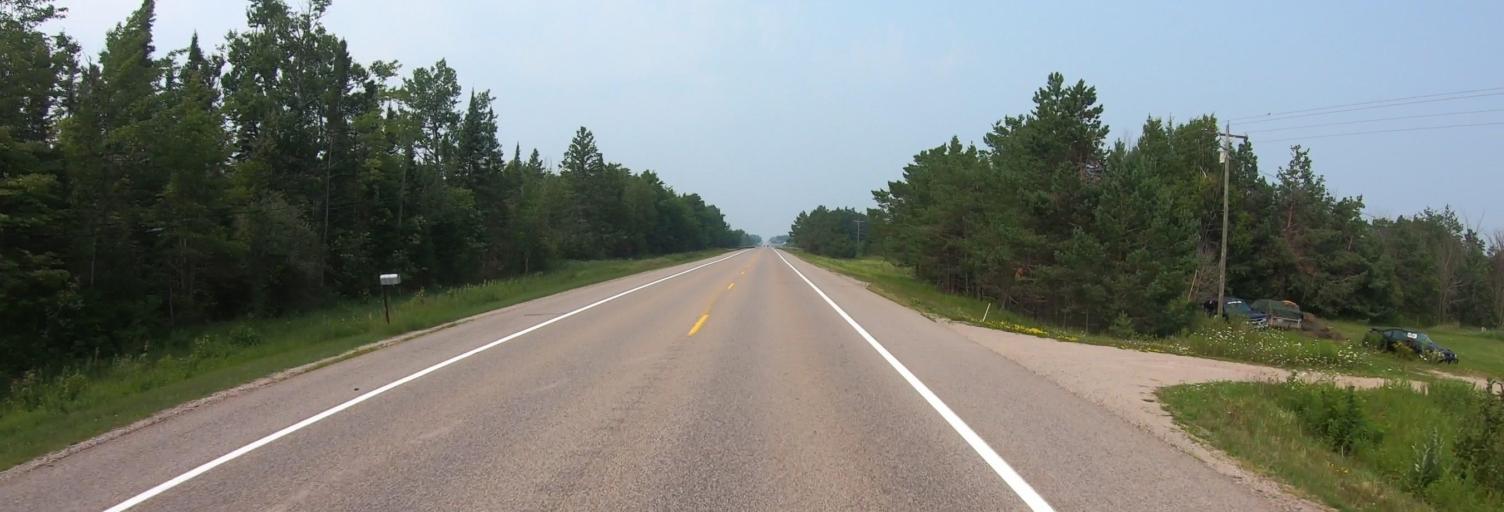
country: US
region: Michigan
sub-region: Chippewa County
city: Sault Ste. Marie
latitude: 46.2689
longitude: -84.3635
